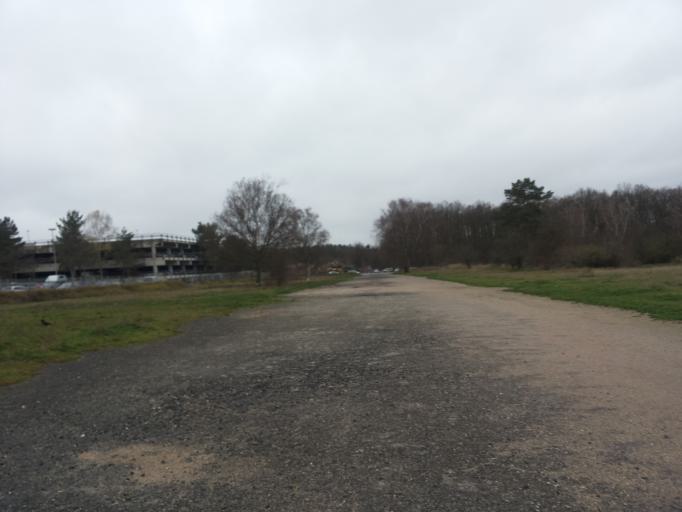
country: DE
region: Bavaria
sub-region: Regierungsbezirk Mittelfranken
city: Wendelstein
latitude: 49.4017
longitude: 11.1644
